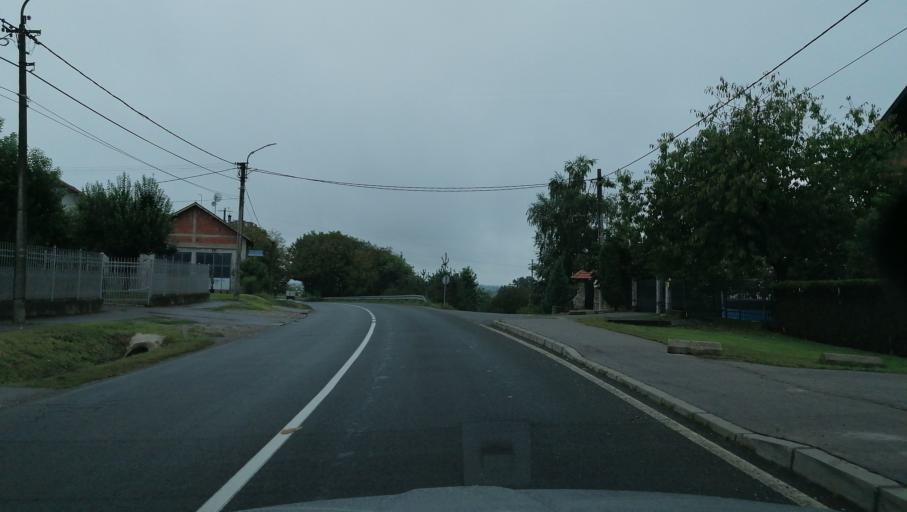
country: RS
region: Central Serbia
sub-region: Rasinski Okrug
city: Krusevac
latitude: 43.5880
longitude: 21.2663
